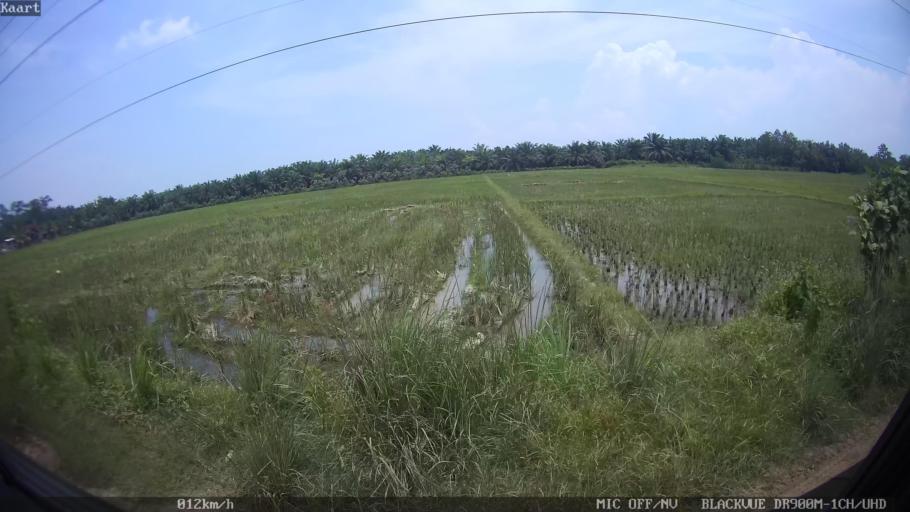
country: ID
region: Lampung
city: Natar
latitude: -5.3148
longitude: 105.2340
